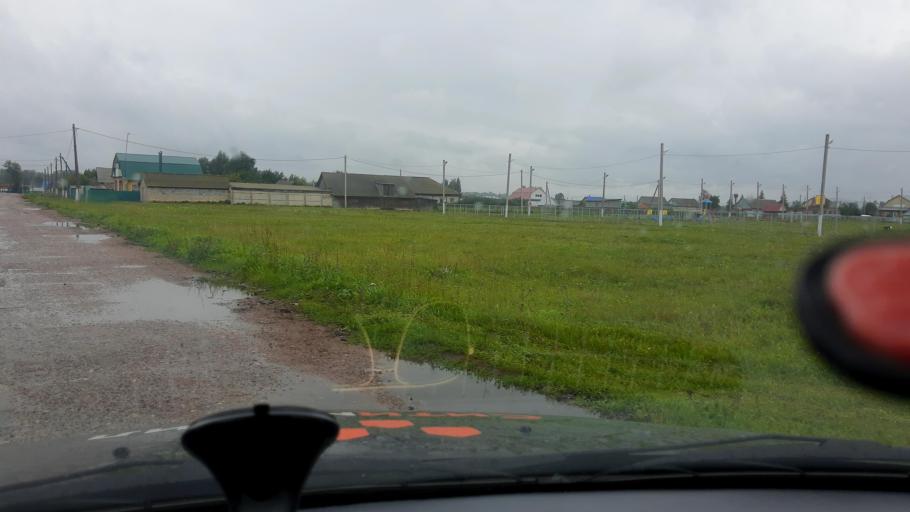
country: RU
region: Bashkortostan
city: Karmaskaly
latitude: 53.9894
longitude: 56.3970
